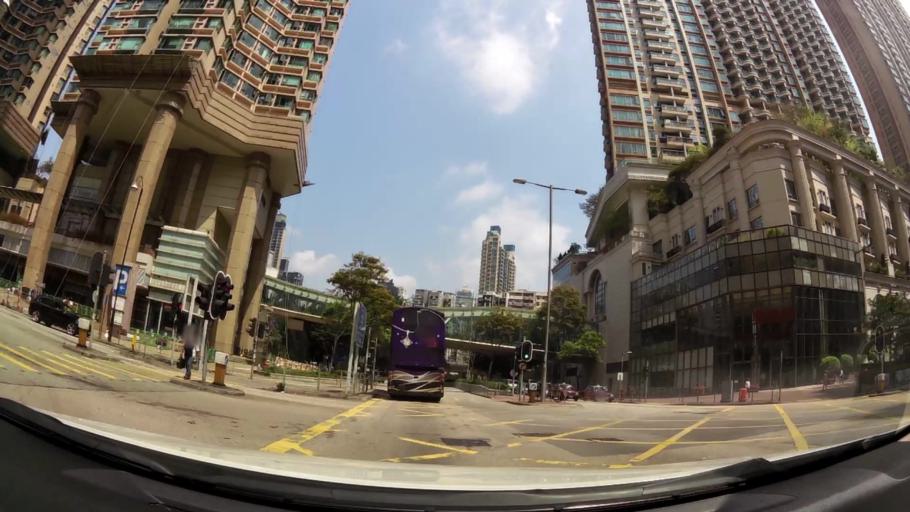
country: HK
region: Sham Shui Po
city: Sham Shui Po
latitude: 22.3169
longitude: 114.1635
